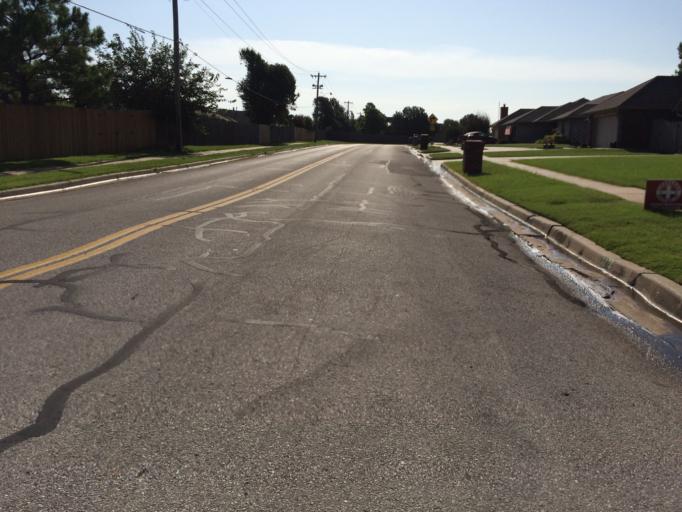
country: US
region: Oklahoma
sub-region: Cleveland County
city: Norman
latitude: 35.2401
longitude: -97.4907
